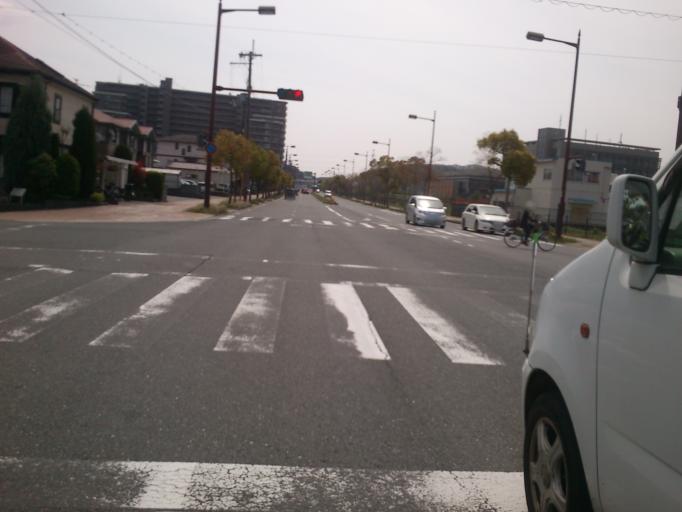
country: JP
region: Kyoto
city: Tanabe
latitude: 34.7632
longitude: 135.7874
